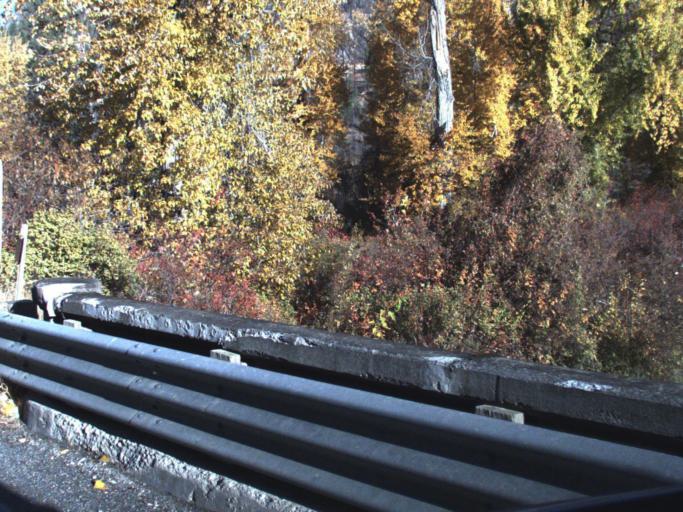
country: US
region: Washington
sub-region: Ferry County
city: Republic
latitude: 48.2685
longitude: -118.7018
